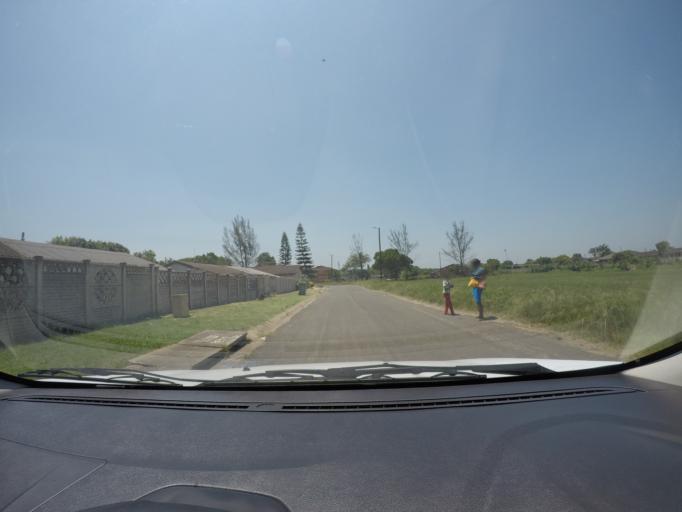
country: ZA
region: KwaZulu-Natal
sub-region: uThungulu District Municipality
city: eSikhawini
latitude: -28.8915
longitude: 31.8871
